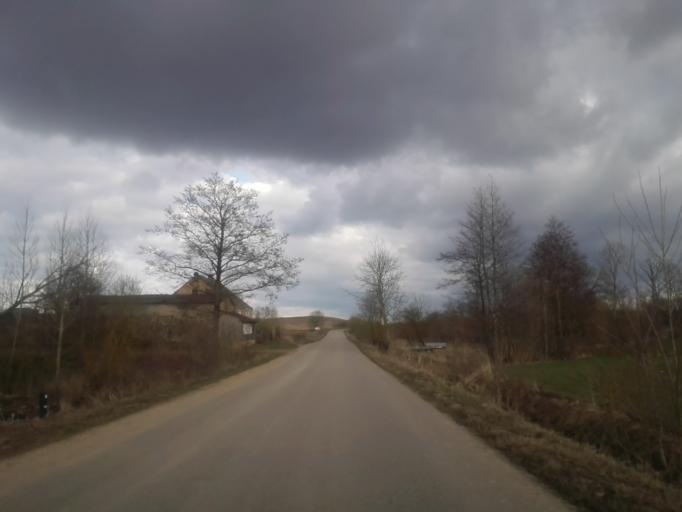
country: PL
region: Podlasie
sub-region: Suwalki
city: Suwalki
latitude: 54.2008
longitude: 22.9673
